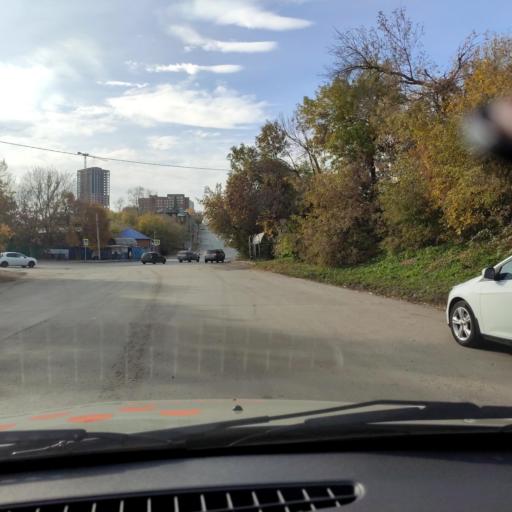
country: RU
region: Bashkortostan
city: Ufa
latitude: 54.7532
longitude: 55.9636
